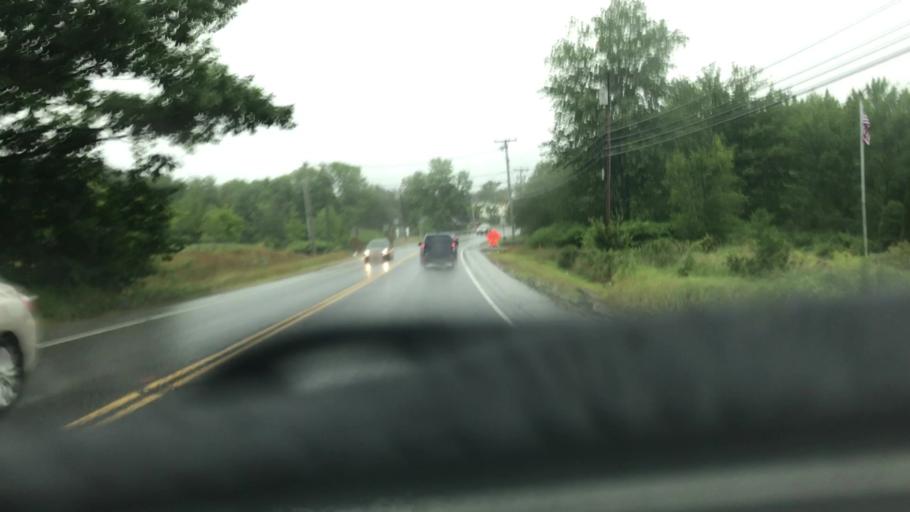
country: US
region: Maine
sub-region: York County
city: Kennebunk
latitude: 43.4014
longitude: -70.5274
